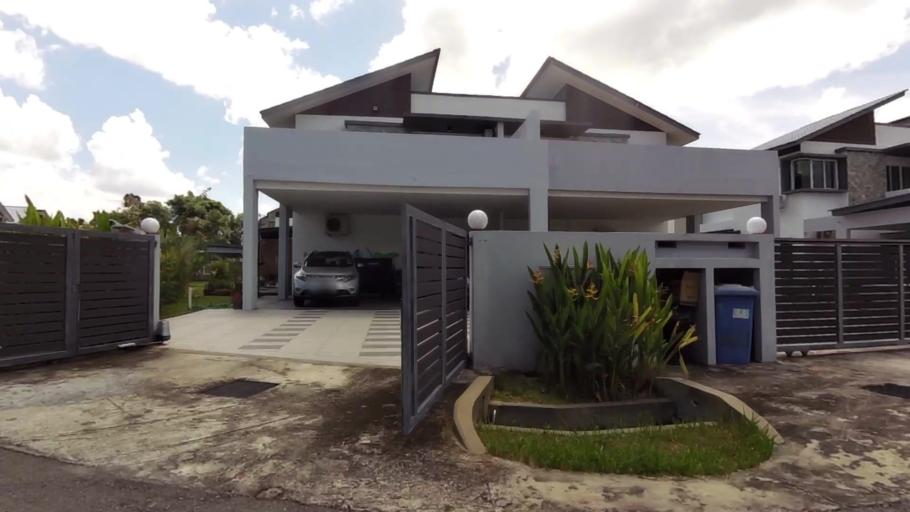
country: BN
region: Brunei and Muara
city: Bandar Seri Begawan
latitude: 4.9439
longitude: 114.9628
